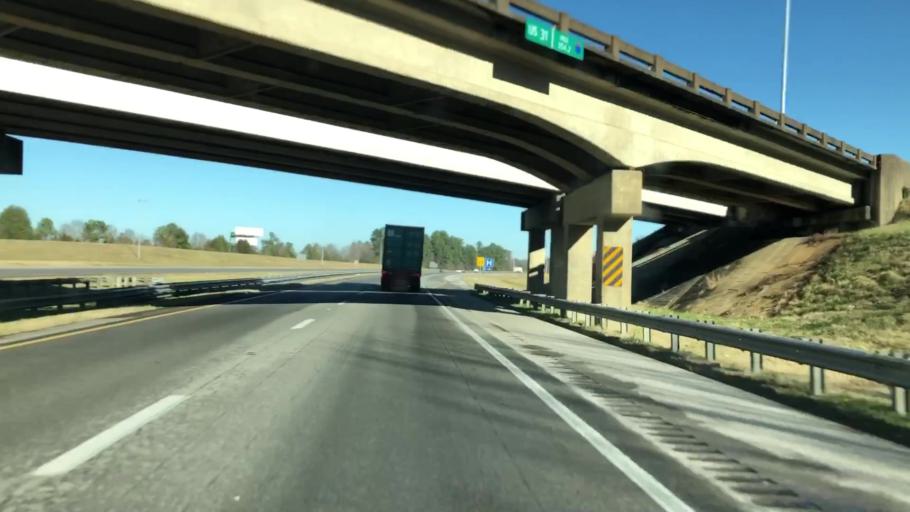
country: US
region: Alabama
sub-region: Limestone County
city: Athens
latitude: 34.8282
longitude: -86.9387
